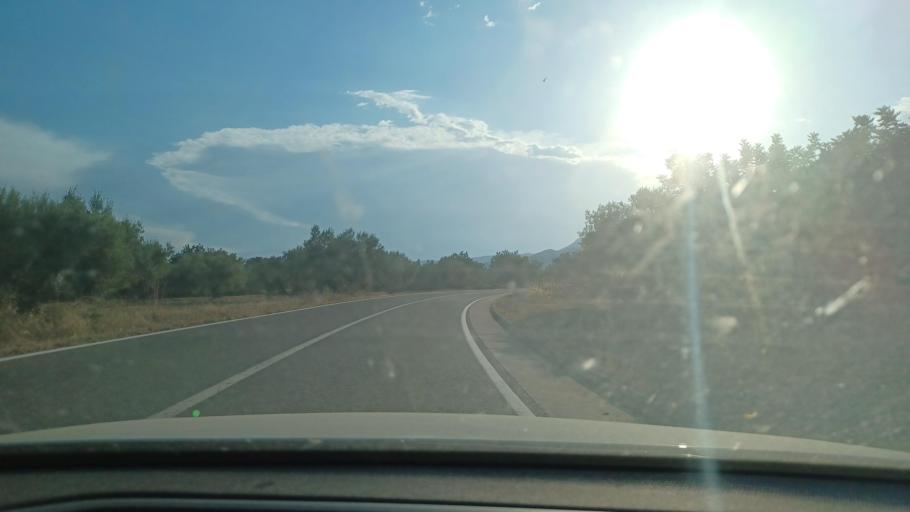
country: ES
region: Catalonia
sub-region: Provincia de Tarragona
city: Mas de Barberans
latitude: 40.7123
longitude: 0.4082
